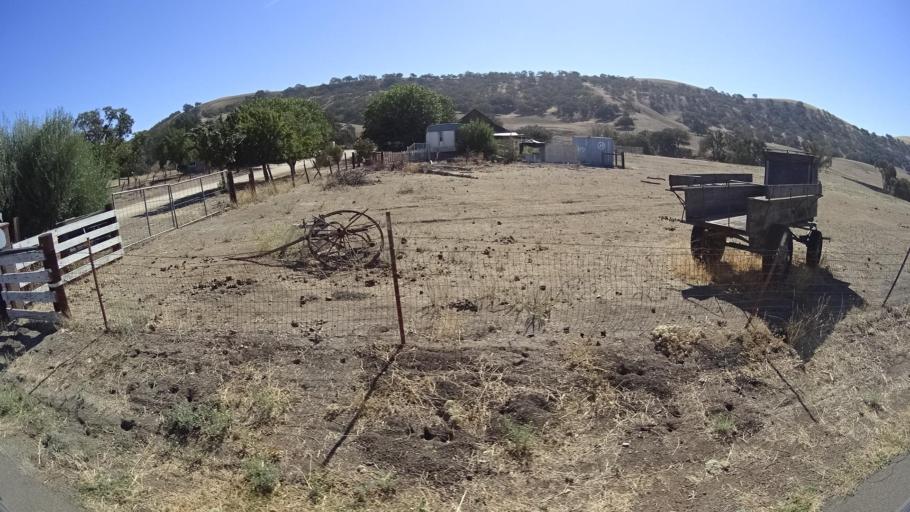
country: US
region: California
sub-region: San Luis Obispo County
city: San Miguel
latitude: 35.7855
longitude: -120.5869
